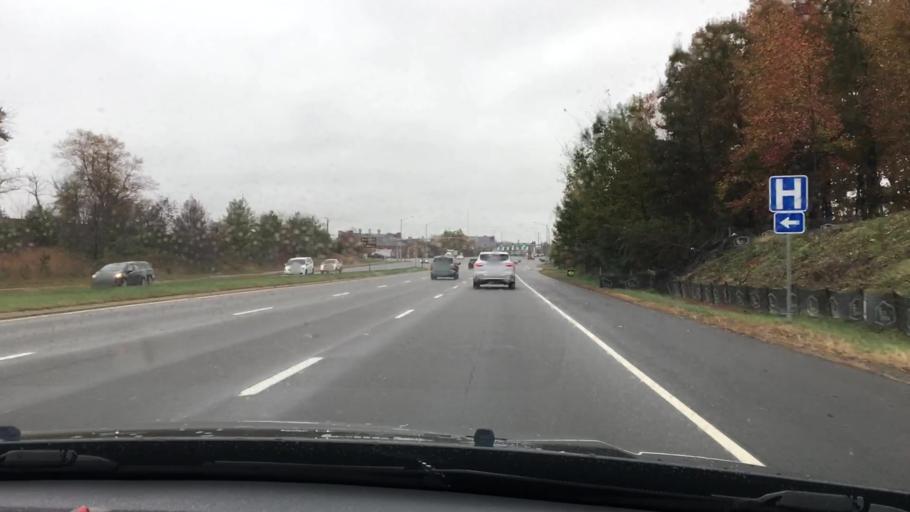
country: US
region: Virginia
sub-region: Fairfax County
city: Lorton
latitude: 38.7017
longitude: -77.2582
